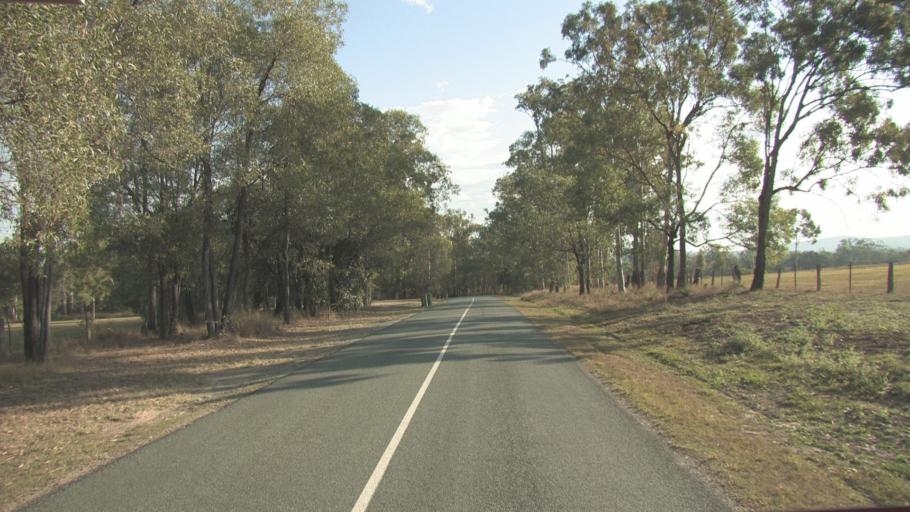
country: AU
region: Queensland
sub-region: Logan
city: Chambers Flat
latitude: -27.8469
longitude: 153.1417
